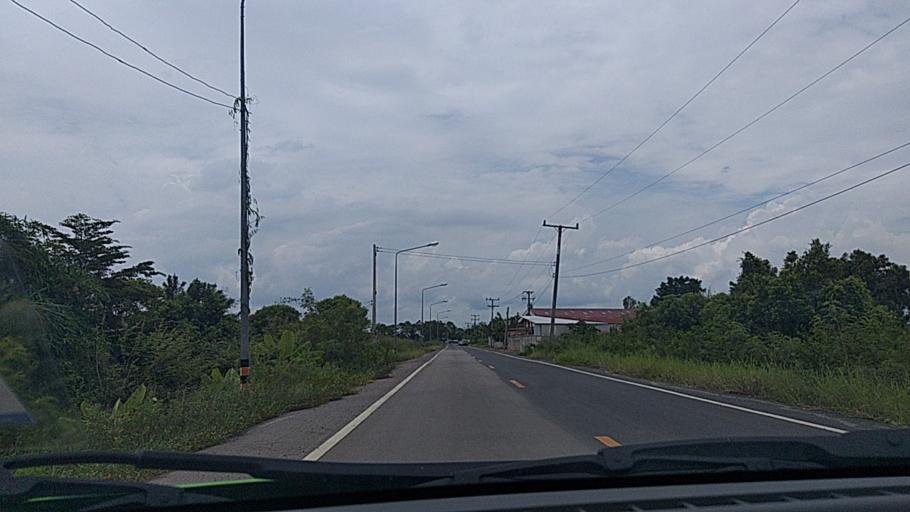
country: TH
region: Nakhon Nayok
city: Ongkharak
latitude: 14.0928
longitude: 100.9549
